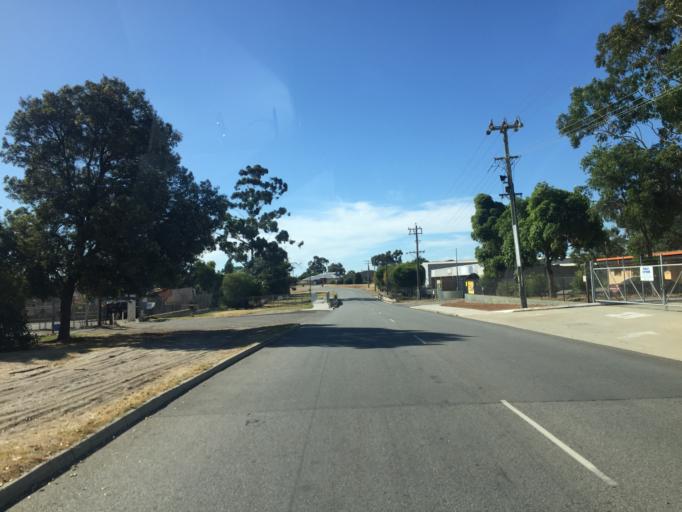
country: AU
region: Western Australia
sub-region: Gosnells
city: Maddington
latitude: -32.0416
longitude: 115.9849
